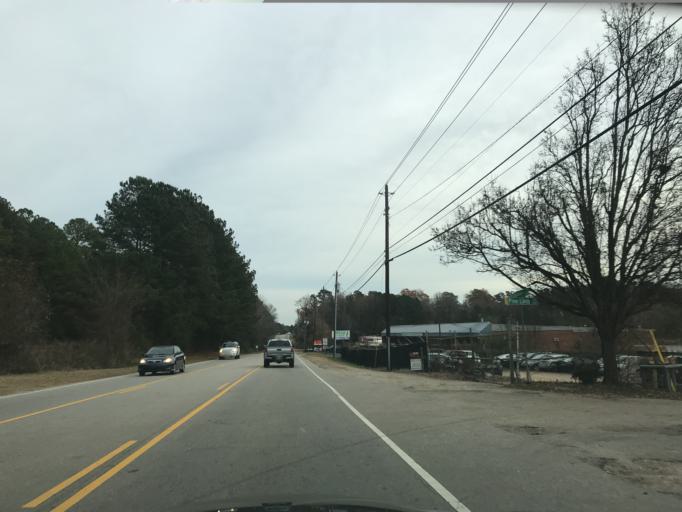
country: US
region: North Carolina
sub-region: Wake County
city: Cary
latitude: 35.7880
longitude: -78.7389
